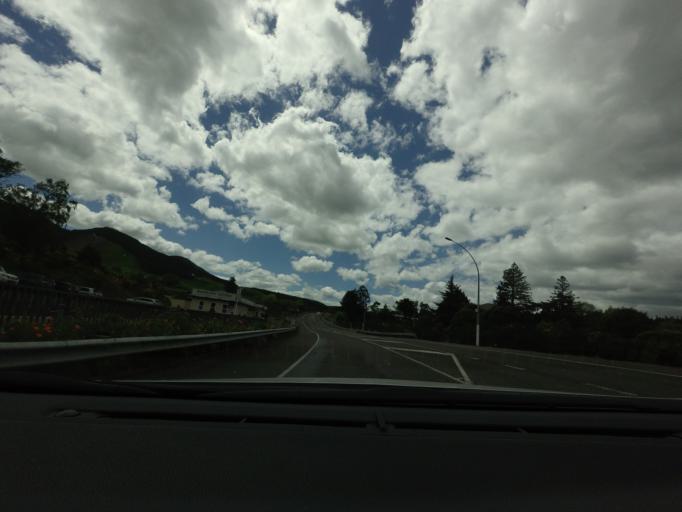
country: NZ
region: Bay of Plenty
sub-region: Rotorua District
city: Rotorua
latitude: -38.3407
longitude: 176.3635
